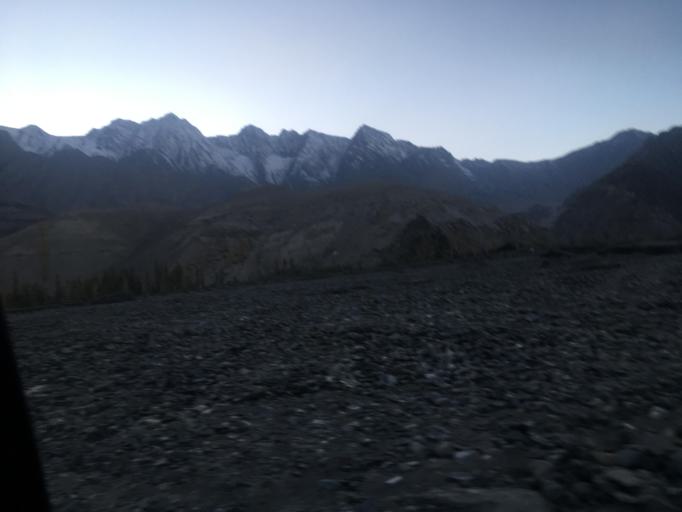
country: PK
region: Gilgit-Baltistan
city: Skardu
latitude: 35.3046
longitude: 75.5379
